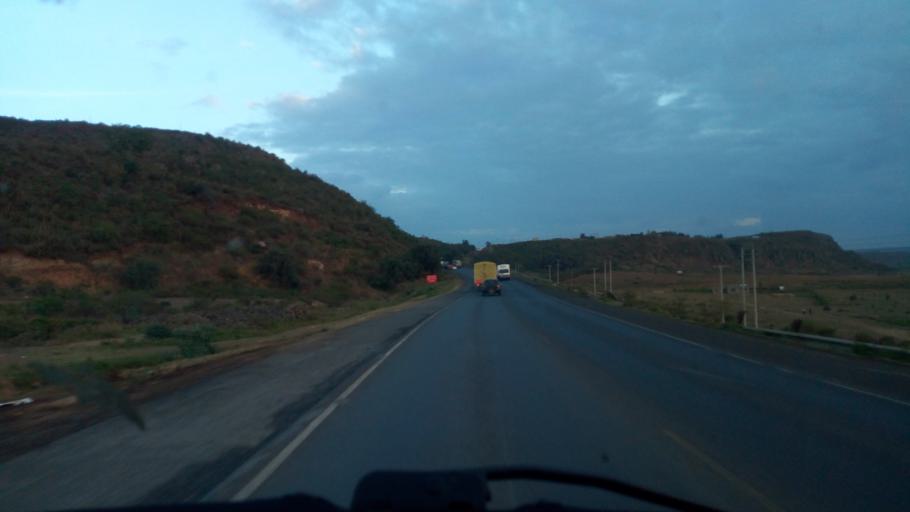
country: KE
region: Nyandarua
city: Ol Kalou
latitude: -0.4831
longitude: 36.3012
